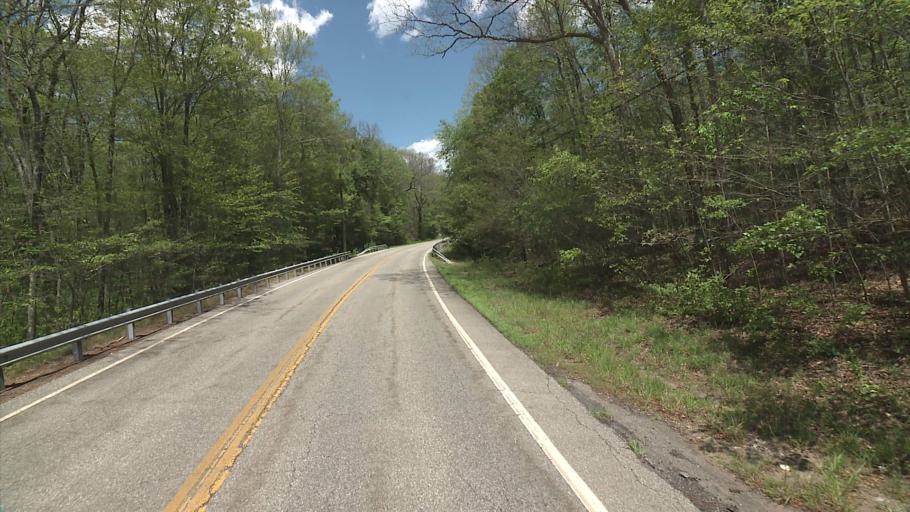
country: US
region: Connecticut
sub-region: Middlesex County
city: Moodus
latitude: 41.5235
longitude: -72.4916
